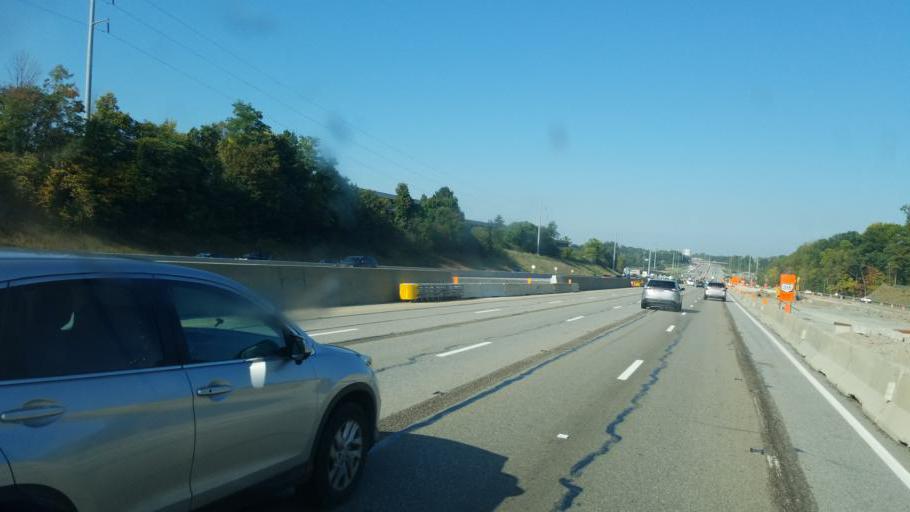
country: US
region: Ohio
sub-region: Franklin County
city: Worthington
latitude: 40.1122
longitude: -83.0222
